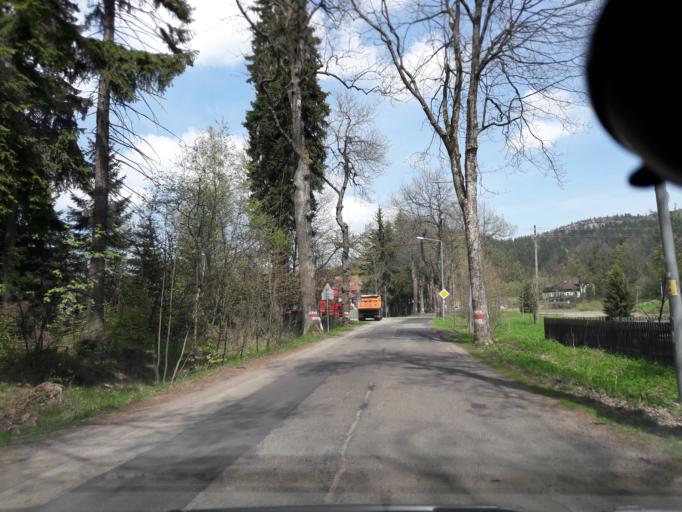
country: CZ
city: Machov
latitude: 50.4728
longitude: 16.3380
